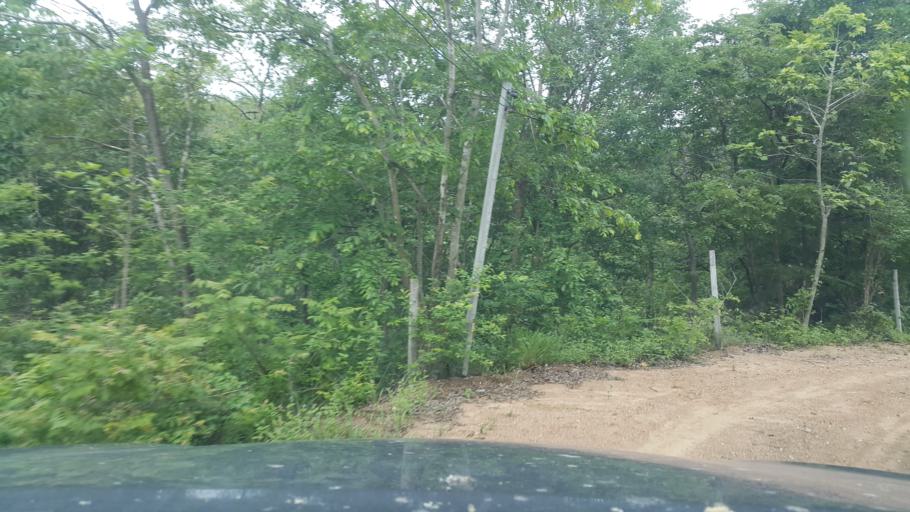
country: TH
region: Chiang Mai
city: Hang Dong
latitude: 18.6930
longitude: 98.8627
